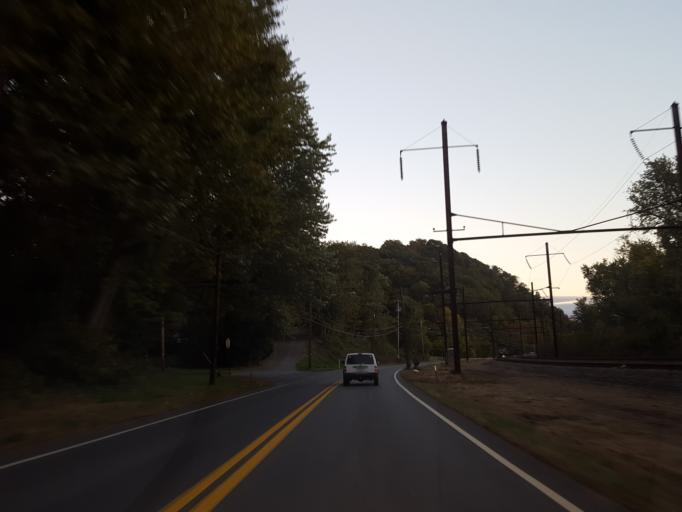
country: US
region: Pennsylvania
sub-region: Lancaster County
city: Columbia
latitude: 40.0239
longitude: -76.4938
